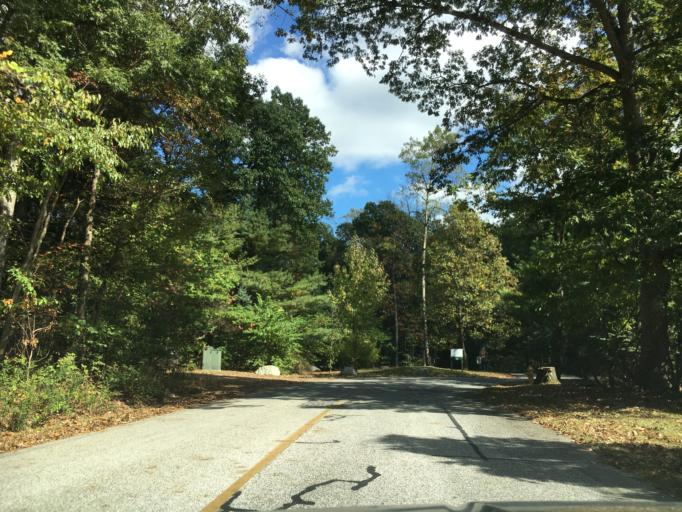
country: US
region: Pennsylvania
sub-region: York County
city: Yorklyn
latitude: 40.0087
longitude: -76.6633
